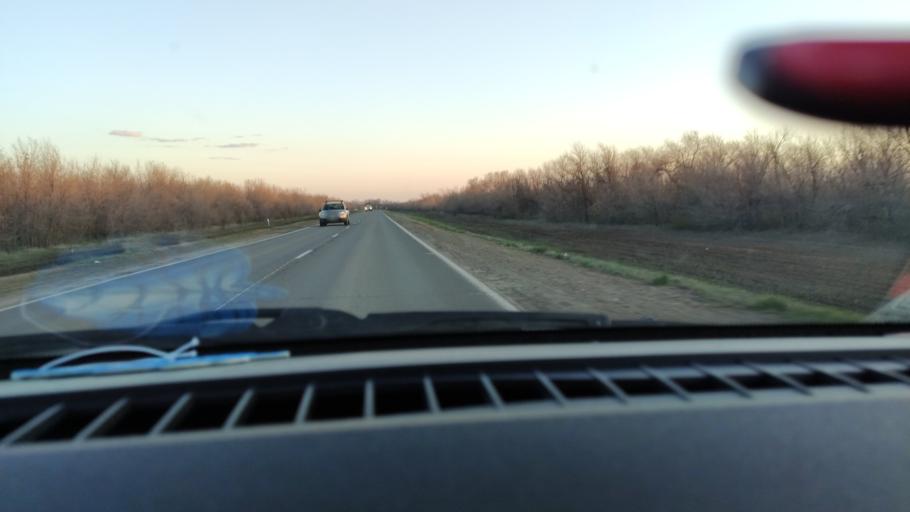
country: RU
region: Saratov
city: Privolzhskiy
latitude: 51.3570
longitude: 46.0436
